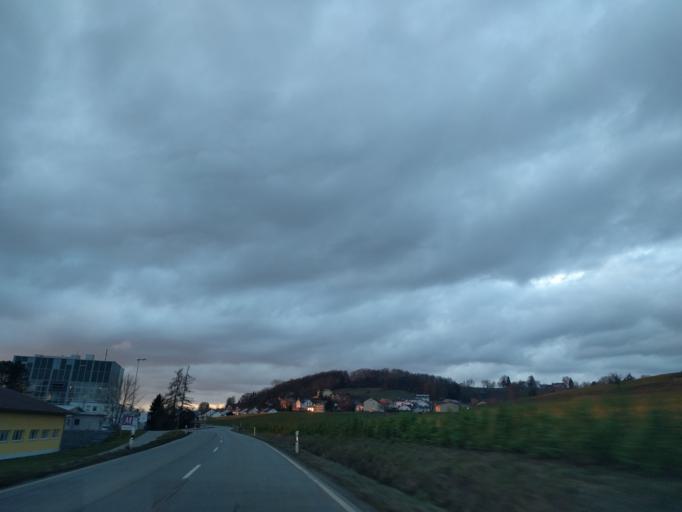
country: DE
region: Bavaria
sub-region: Lower Bavaria
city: Winzer
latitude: 48.7170
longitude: 13.0907
